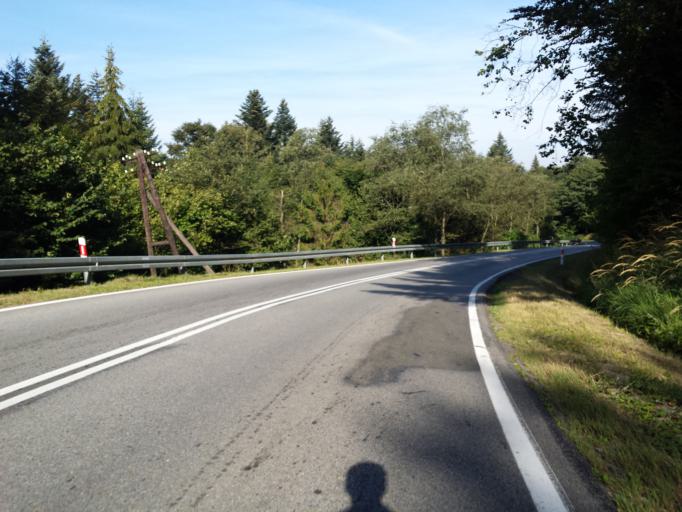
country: PL
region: Subcarpathian Voivodeship
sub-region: Powiat leski
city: Cisna
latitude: 49.2441
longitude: 22.2922
